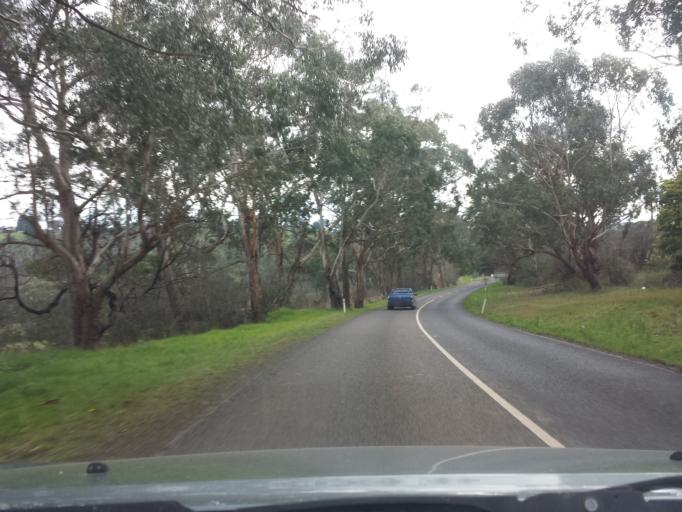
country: AU
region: Victoria
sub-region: Yarra Ranges
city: Woori Yallock
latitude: -37.7908
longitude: 145.4678
